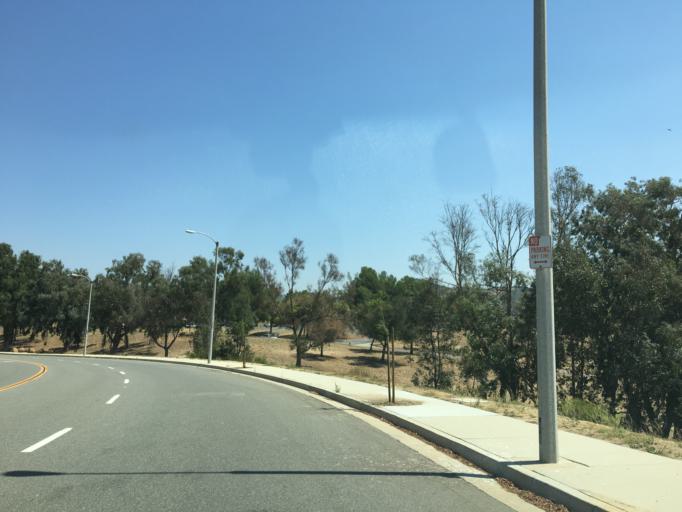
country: US
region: California
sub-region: Los Angeles County
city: Castaic
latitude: 34.5023
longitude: -118.6162
